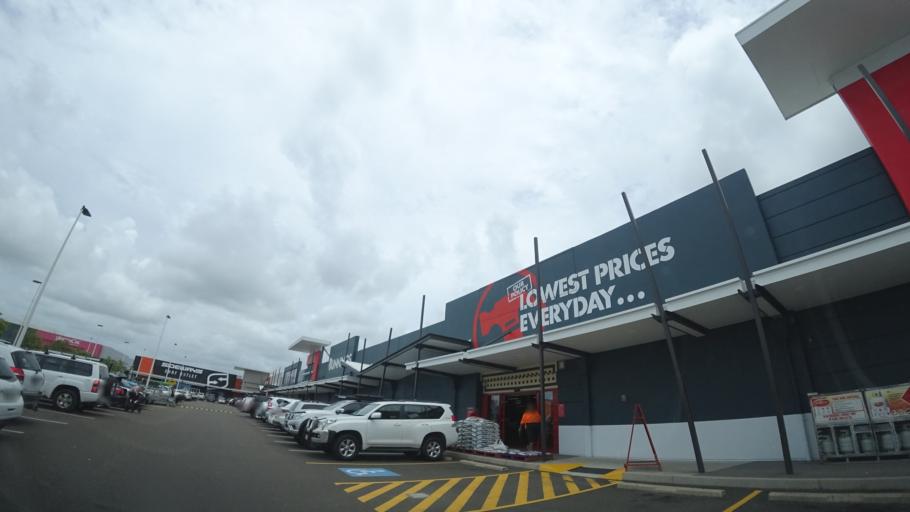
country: AU
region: Queensland
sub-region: Sunshine Coast
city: Dicky Beach
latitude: -26.7365
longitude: 153.1192
